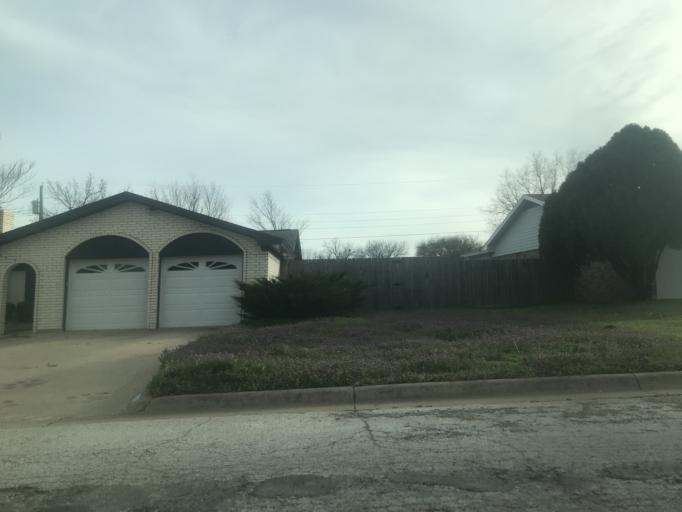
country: US
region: Texas
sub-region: Taylor County
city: Abilene
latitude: 32.3956
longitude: -99.7547
